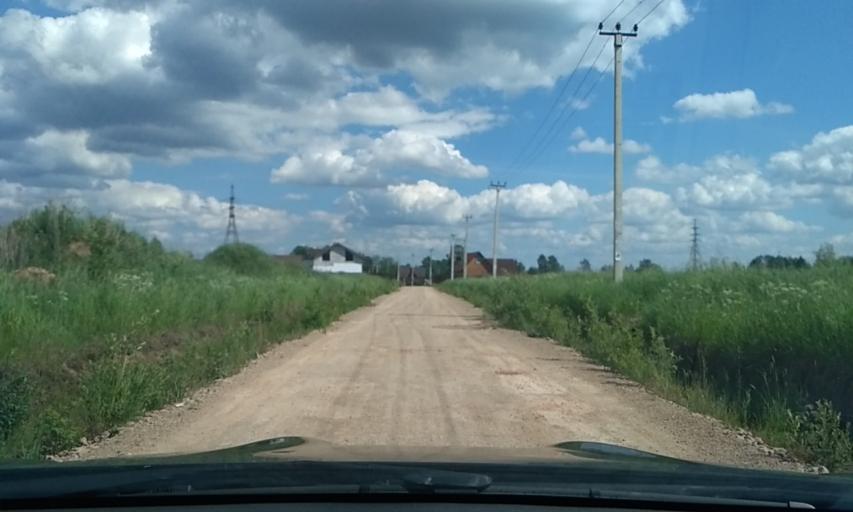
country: RU
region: Leningrad
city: Otradnoye
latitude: 59.8123
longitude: 30.8293
